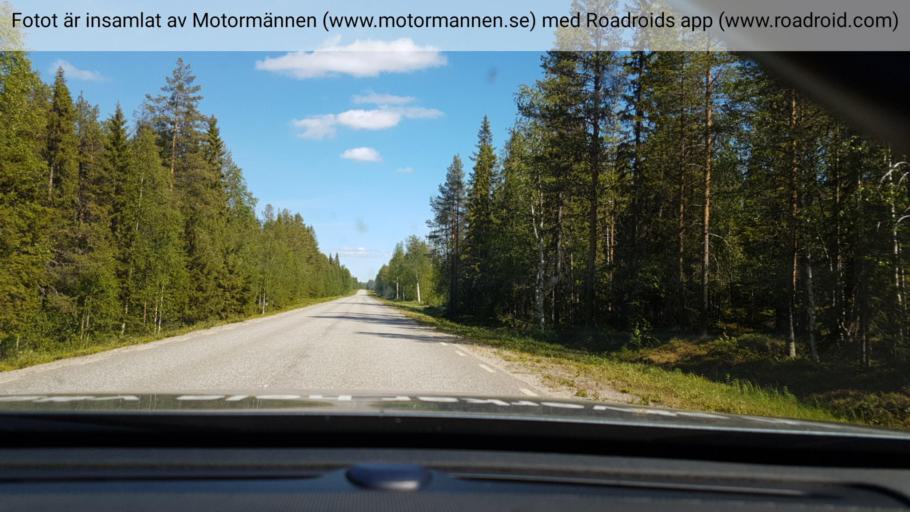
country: SE
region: Vaesterbotten
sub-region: Lycksele Kommun
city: Soderfors
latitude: 64.6340
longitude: 17.9431
